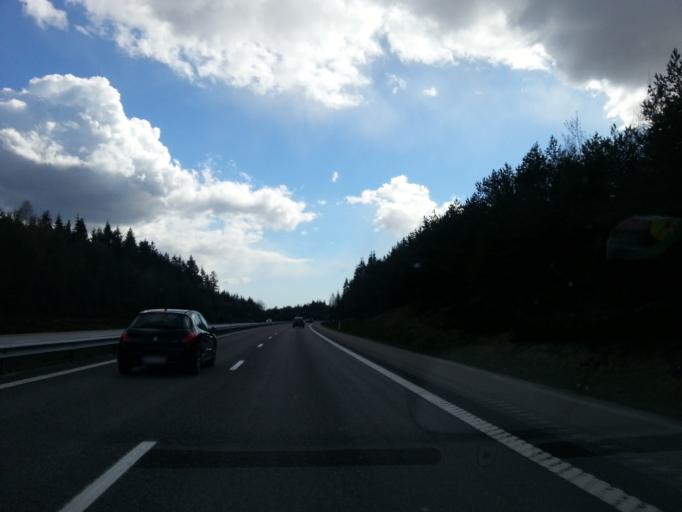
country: SE
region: Vaestra Goetaland
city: Svanesund
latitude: 58.1307
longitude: 11.8855
